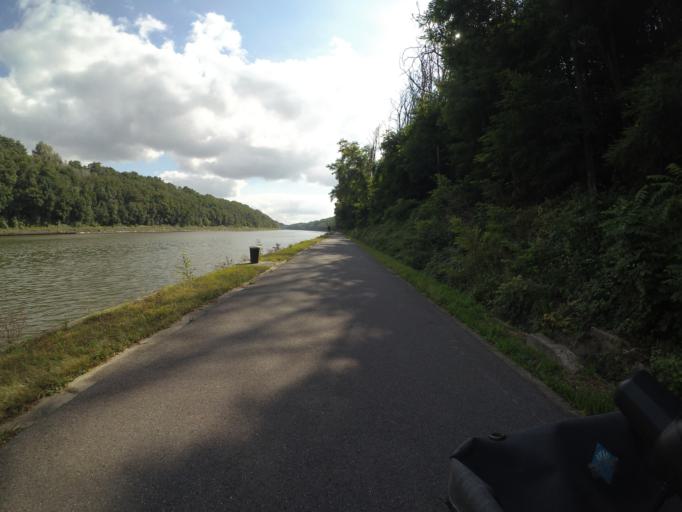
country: BE
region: Flanders
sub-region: Provincie Limburg
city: Lanaken
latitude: 50.8480
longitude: 5.6363
